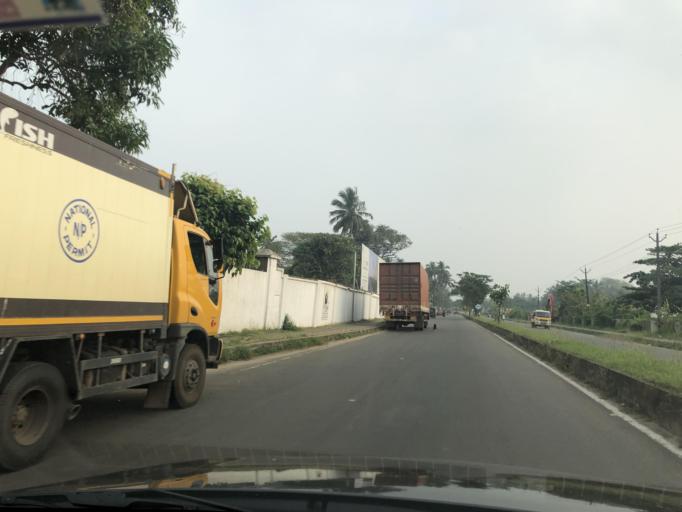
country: IN
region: Kerala
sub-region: Kozhikode
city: Kozhikode
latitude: 11.2888
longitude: 75.7593
